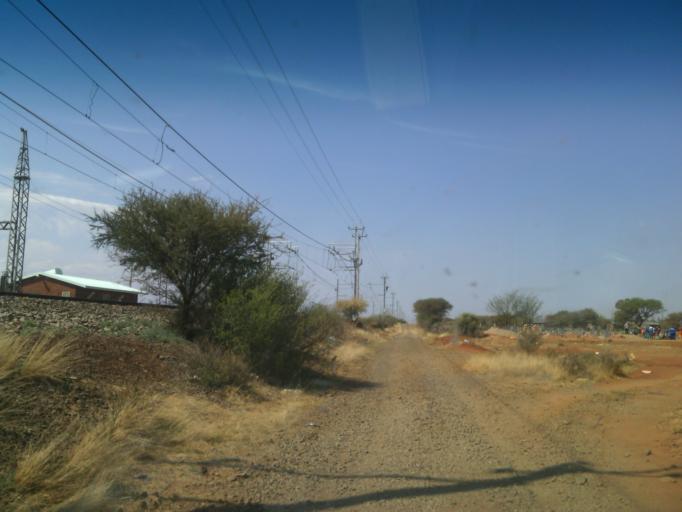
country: ZA
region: Northern Cape
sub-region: Frances Baard District Municipality
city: Barkly West
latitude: -28.5174
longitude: 24.4999
